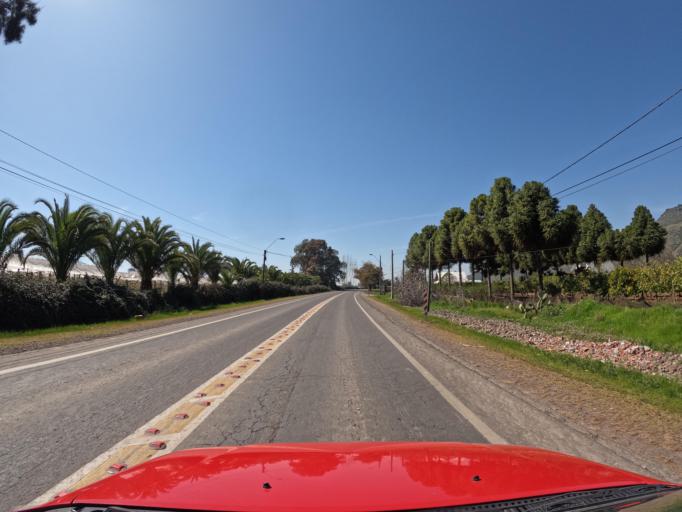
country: CL
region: Maule
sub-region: Provincia de Curico
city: Rauco
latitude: -35.0077
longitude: -71.4092
